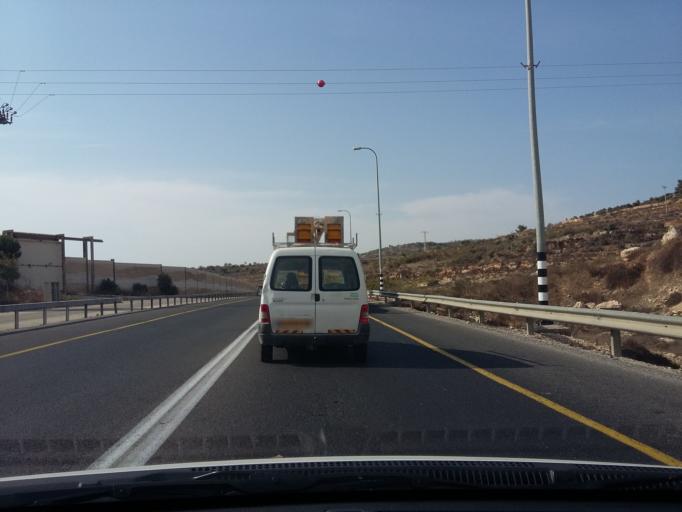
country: PS
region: West Bank
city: Al Khadir
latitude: 31.6989
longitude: 35.1560
